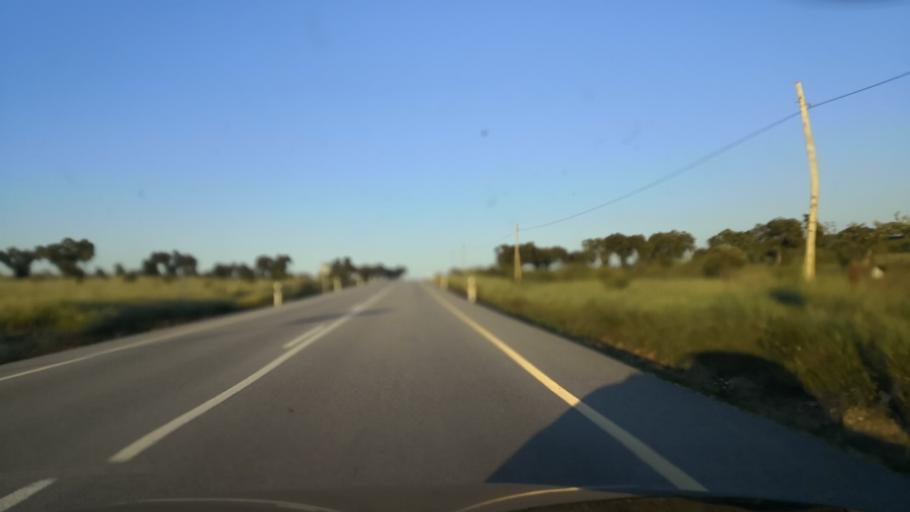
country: ES
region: Extremadura
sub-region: Provincia de Caceres
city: Salorino
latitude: 39.5136
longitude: -7.0768
